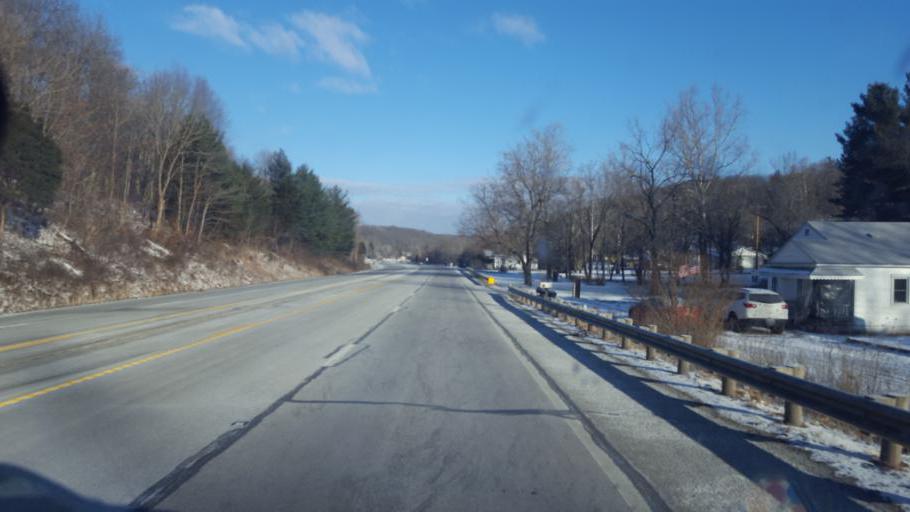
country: US
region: Ohio
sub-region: Pike County
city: Waverly
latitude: 39.2264
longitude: -82.9829
